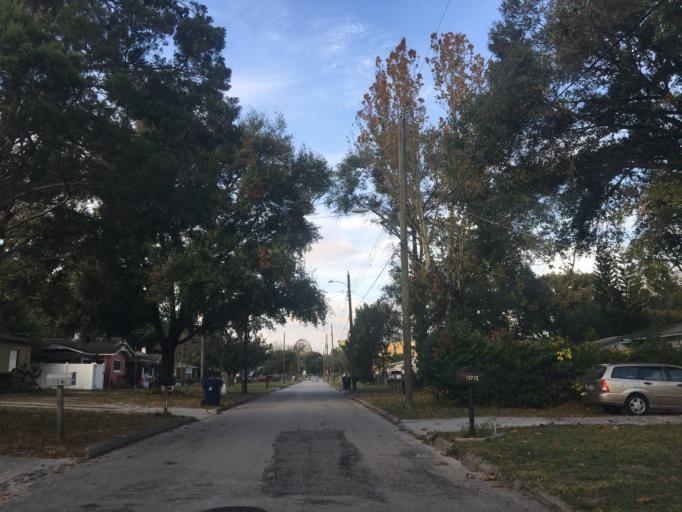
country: US
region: Florida
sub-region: Hillsborough County
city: Temple Terrace
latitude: 28.0300
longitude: -82.4238
